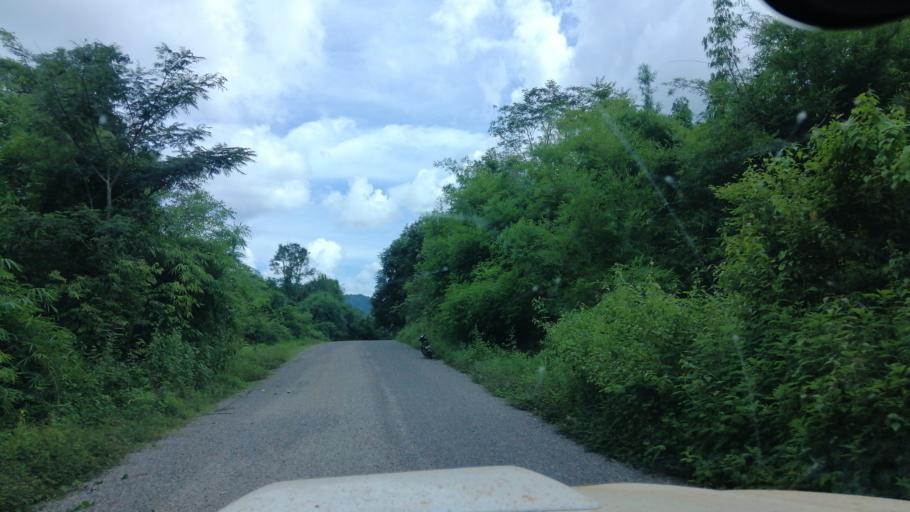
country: TH
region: Uttaradit
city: Ban Khok
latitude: 18.3442
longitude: 101.1380
